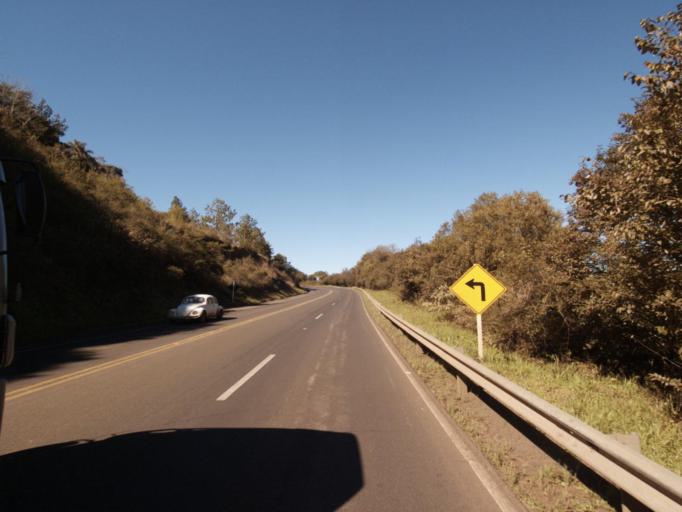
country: BR
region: Santa Catarina
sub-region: Sao Lourenco Do Oeste
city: Sao Lourenco dOeste
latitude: -26.8249
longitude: -53.1028
